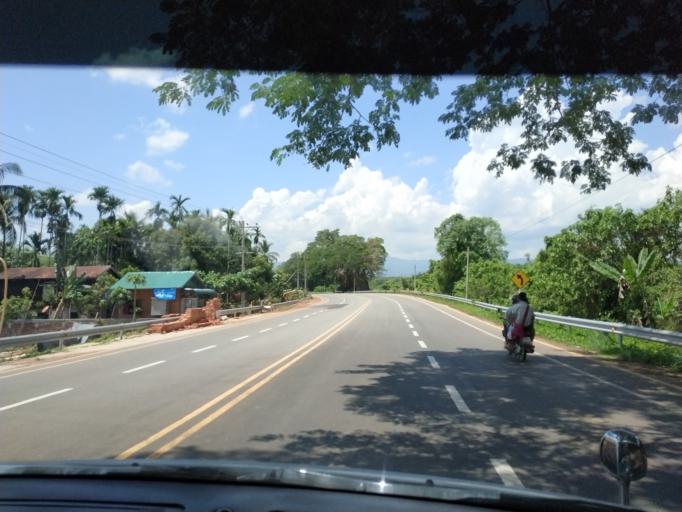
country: MM
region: Mon
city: Kyaikto
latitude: 17.3463
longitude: 97.0377
